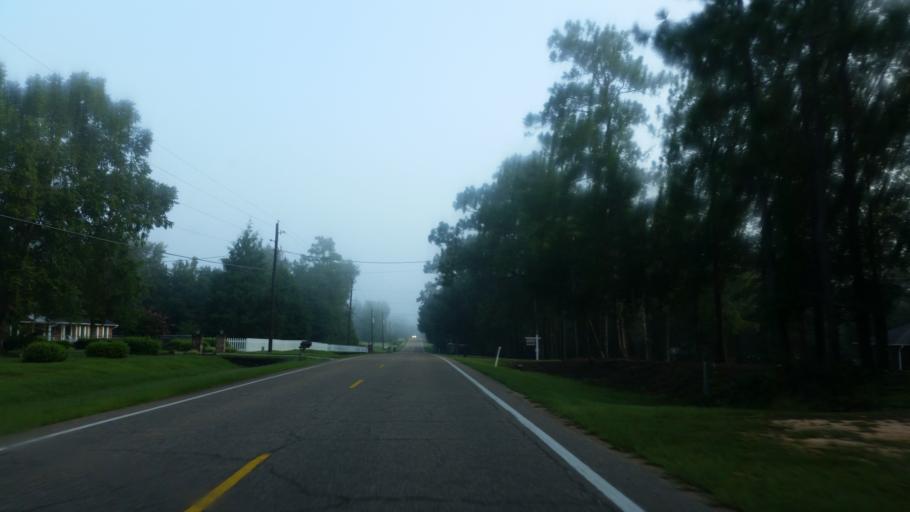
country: US
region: Florida
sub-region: Escambia County
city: Molino
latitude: 30.7306
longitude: -87.3444
